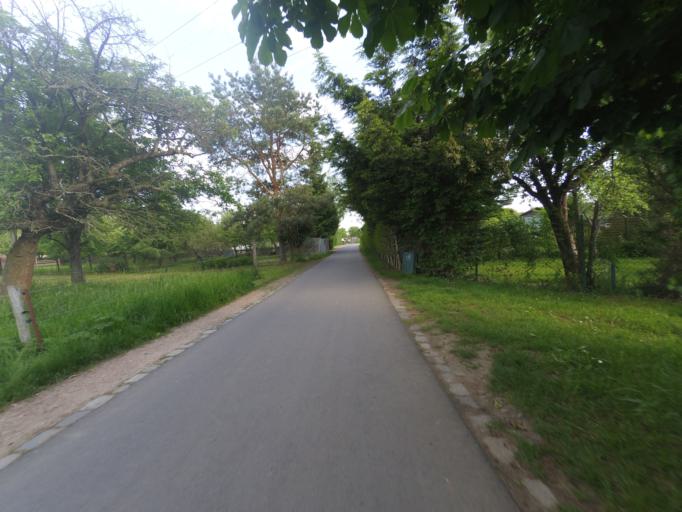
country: DE
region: Saxony
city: Radebeul
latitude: 51.1025
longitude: 13.6339
